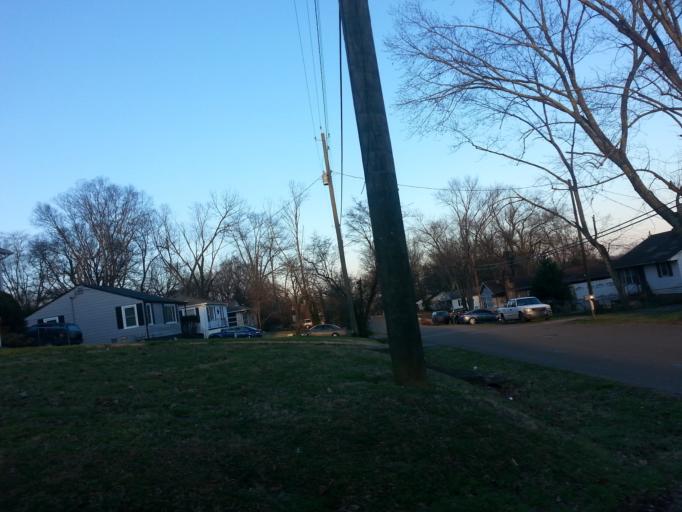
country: US
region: Tennessee
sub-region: Knox County
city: Knoxville
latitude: 36.0190
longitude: -83.8681
